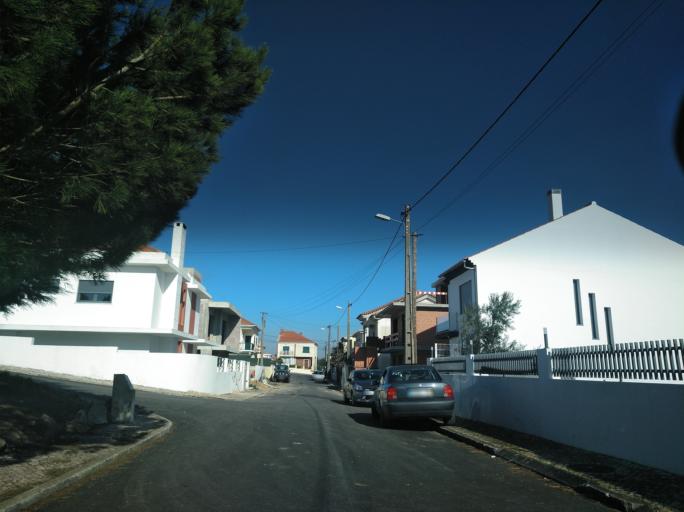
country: PT
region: Lisbon
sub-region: Odivelas
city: Canecas
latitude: 38.8015
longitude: -9.2207
